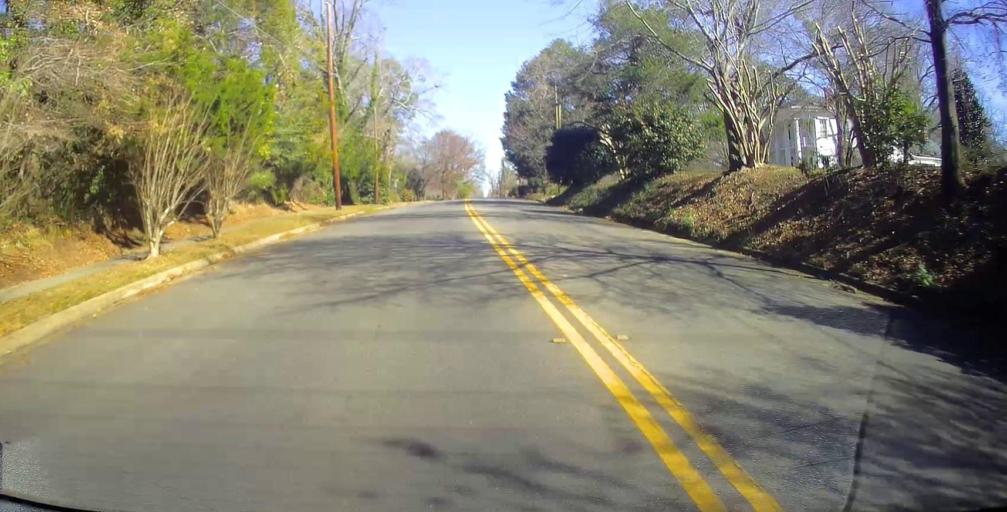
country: US
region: Georgia
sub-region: Macon County
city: Marshallville
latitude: 32.4565
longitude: -83.9544
